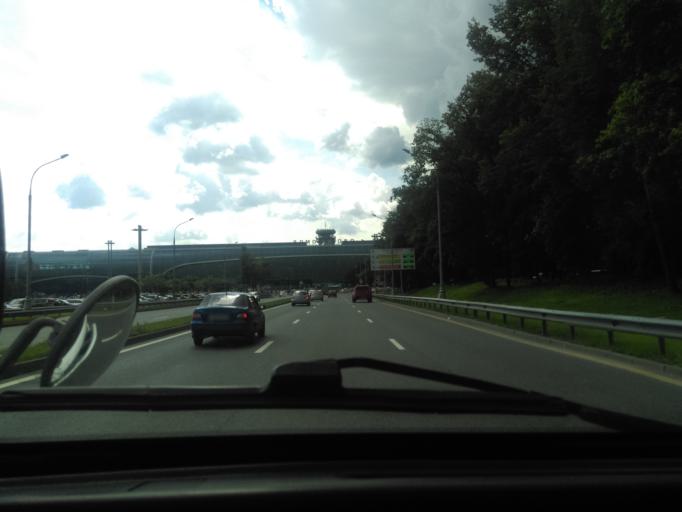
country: RU
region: Moskovskaya
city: Yakovlevskoye
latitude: 55.4168
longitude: 37.8970
